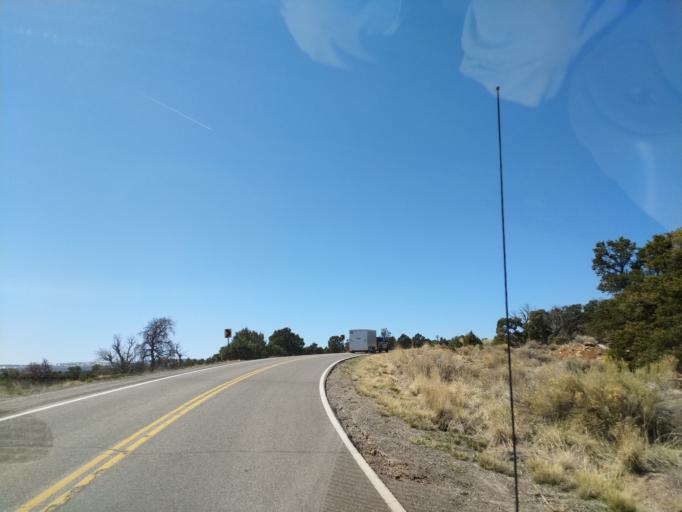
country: US
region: Colorado
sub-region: Mesa County
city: Redlands
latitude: 39.0190
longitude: -108.6600
